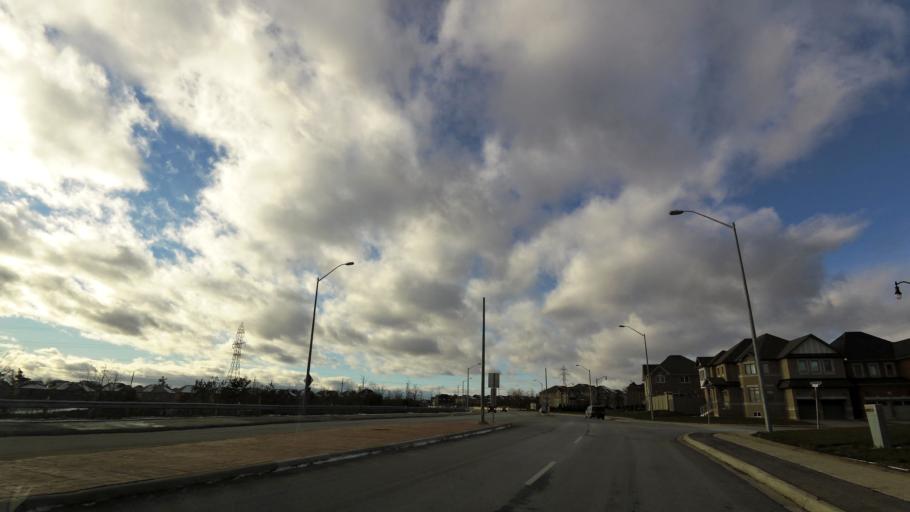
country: CA
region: Ontario
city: Brampton
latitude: 43.6534
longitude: -79.7688
